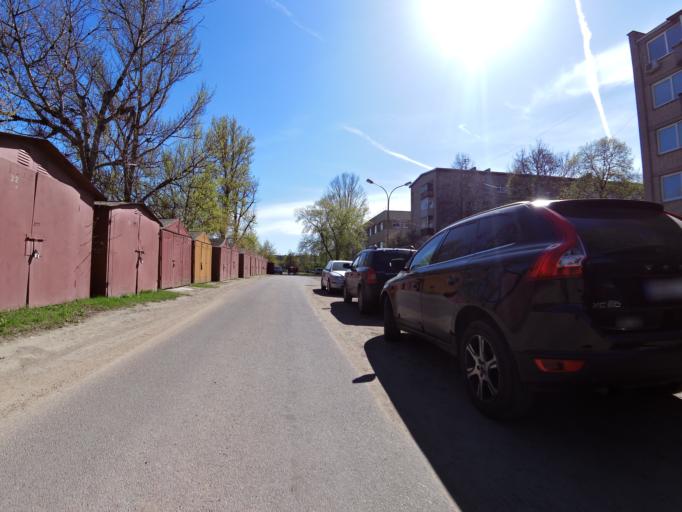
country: LT
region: Vilnius County
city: Vilkpede
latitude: 54.6695
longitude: 25.2540
